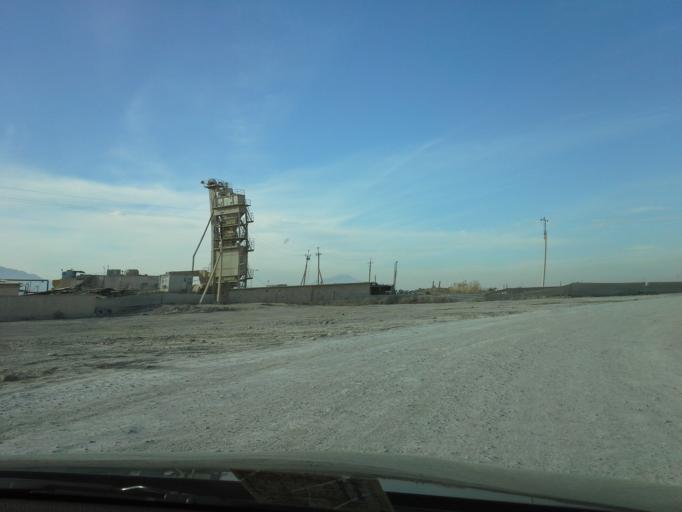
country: TM
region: Ahal
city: Abadan
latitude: 38.0282
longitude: 58.1632
